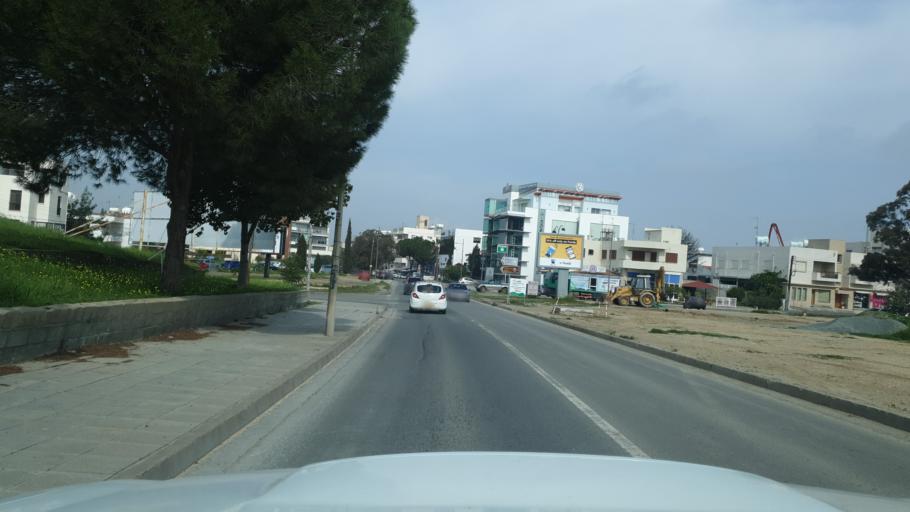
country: CY
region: Lefkosia
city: Nicosia
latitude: 35.1534
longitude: 33.3172
